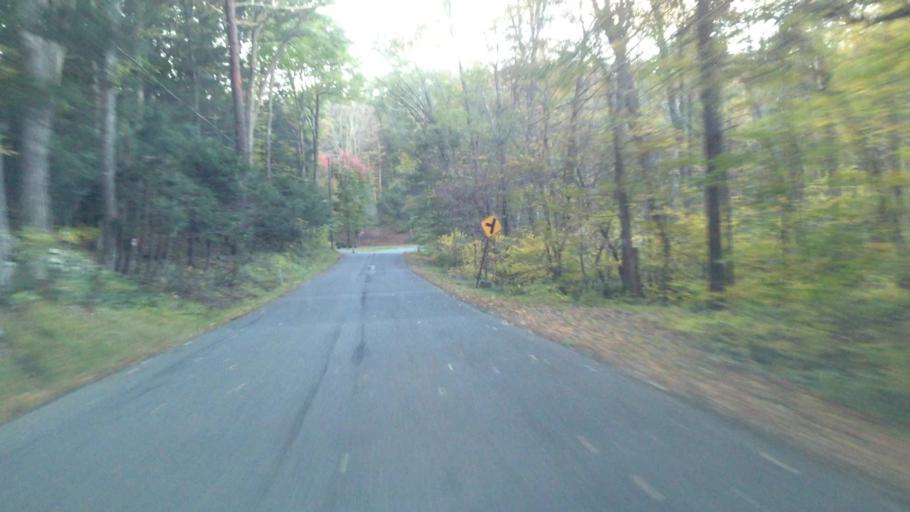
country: US
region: New York
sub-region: Dutchess County
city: Hyde Park
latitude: 41.8084
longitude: -73.9818
